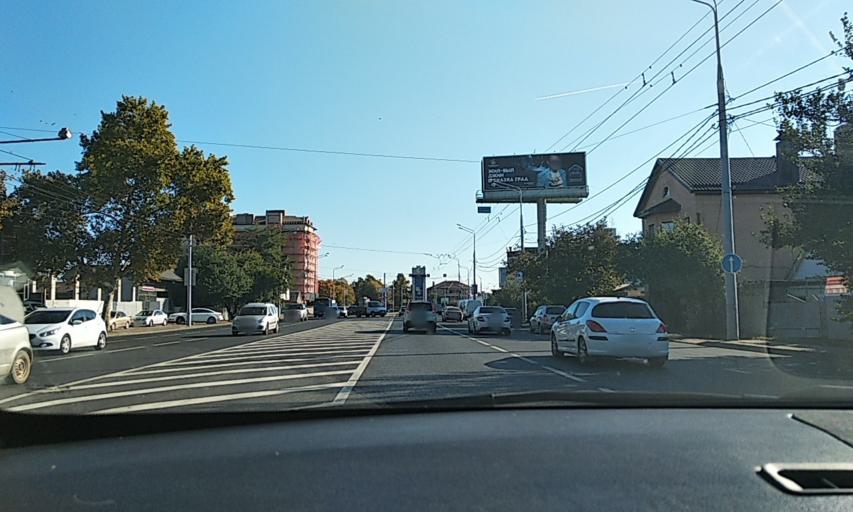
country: RU
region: Krasnodarskiy
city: Pashkovskiy
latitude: 45.0153
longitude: 39.0904
